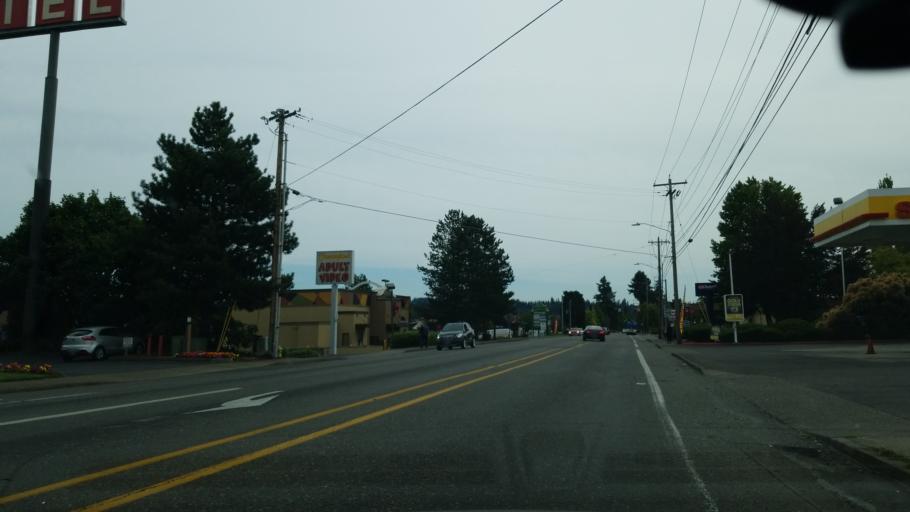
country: US
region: Oregon
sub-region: Clackamas County
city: Clackamas
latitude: 45.4071
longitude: -122.5689
